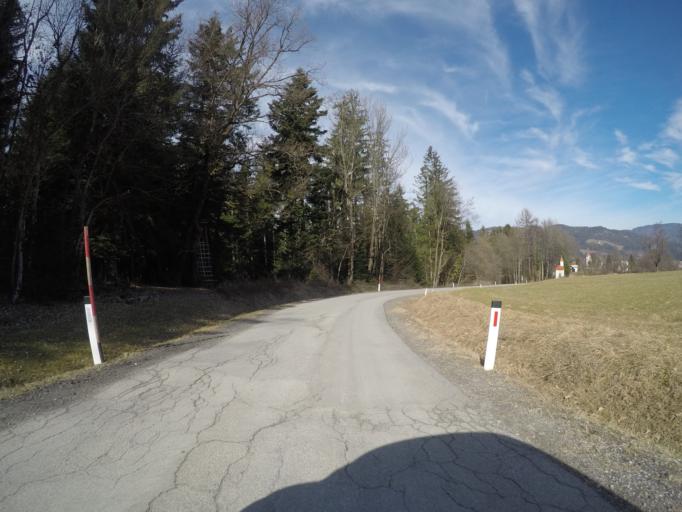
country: SI
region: Lovrenc na Pohorju
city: Lovrenc na Pohorju
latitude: 46.5309
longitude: 15.3762
